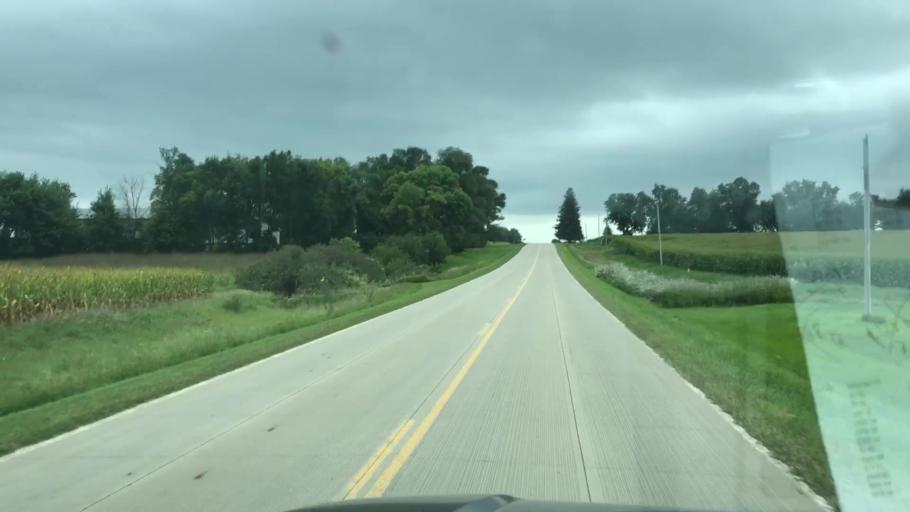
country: US
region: Iowa
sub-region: Sioux County
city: Alton
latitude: 43.1115
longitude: -95.9787
